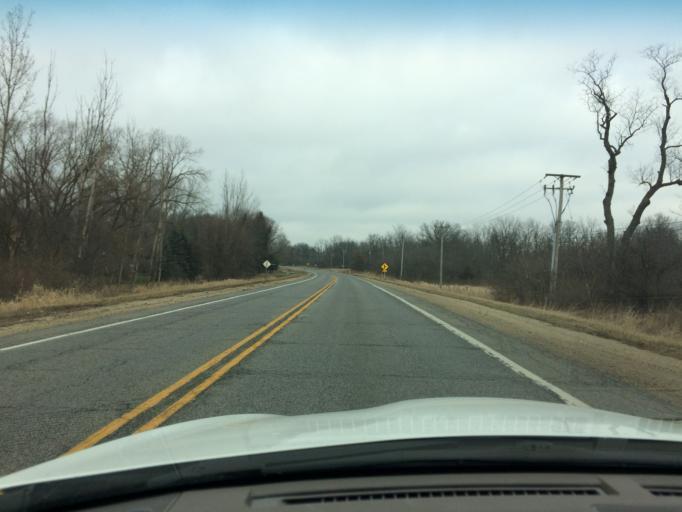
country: US
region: Illinois
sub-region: Kane County
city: Sugar Grove
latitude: 41.8053
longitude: -88.4604
